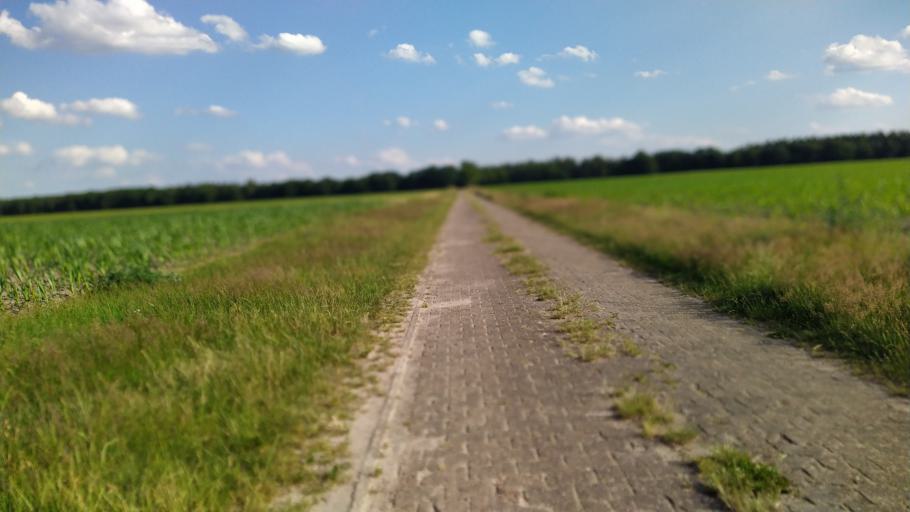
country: DE
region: Lower Saxony
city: Lintig
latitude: 53.6026
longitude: 8.8928
